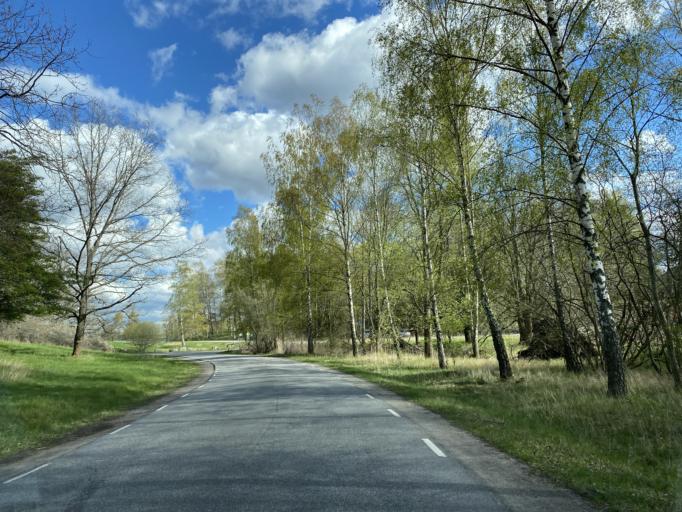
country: SE
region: Stockholm
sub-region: Stockholms Kommun
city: OEstermalm
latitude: 59.3623
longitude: 18.0883
